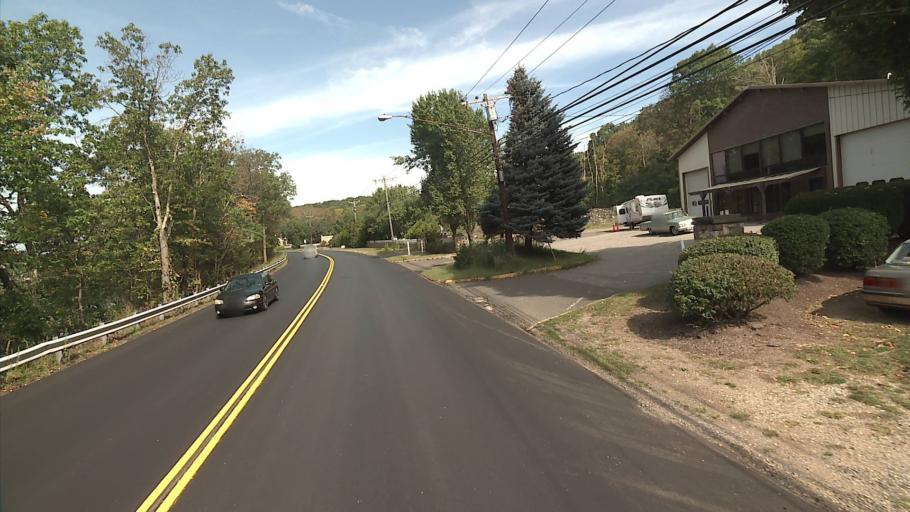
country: US
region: Connecticut
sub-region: New Haven County
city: Ansonia
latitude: 41.3615
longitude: -73.1380
